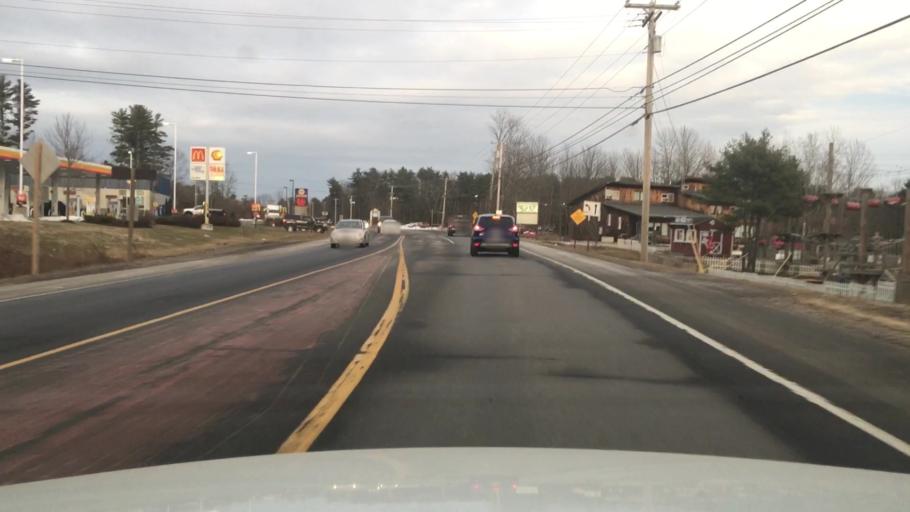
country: US
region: Maine
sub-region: Lincoln County
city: Wiscasset
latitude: 43.9717
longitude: -69.7127
